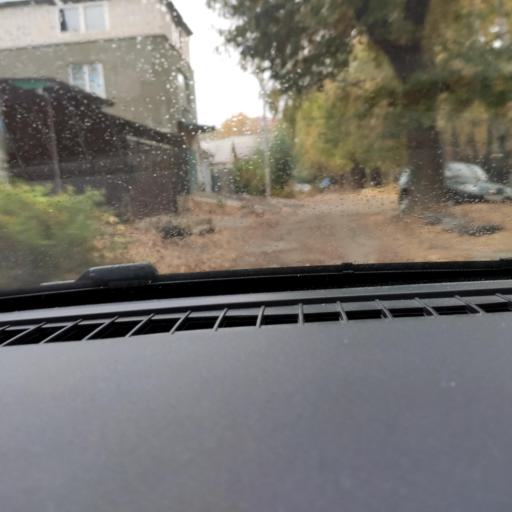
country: RU
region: Voronezj
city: Voronezh
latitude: 51.6954
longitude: 39.2178
